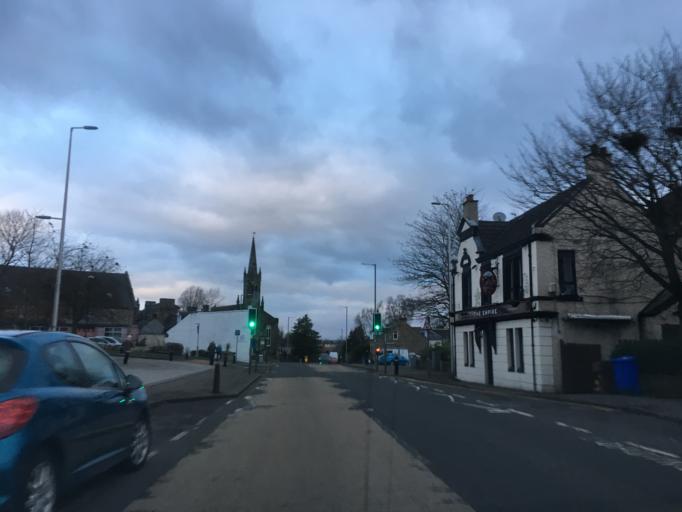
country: GB
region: Scotland
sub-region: Stirling
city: Bannockburn
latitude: 56.0902
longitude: -3.9116
